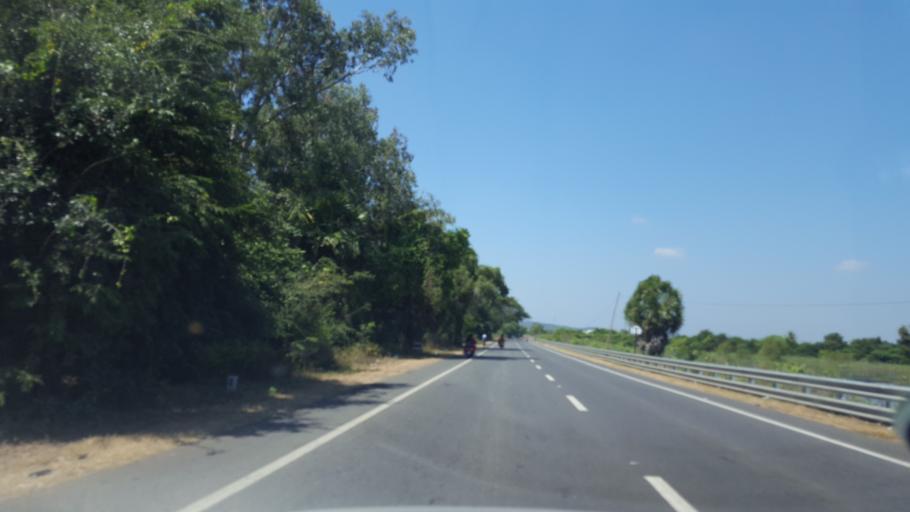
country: IN
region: Tamil Nadu
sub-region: Kancheepuram
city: Karumbakkam
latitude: 12.6282
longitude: 80.0511
